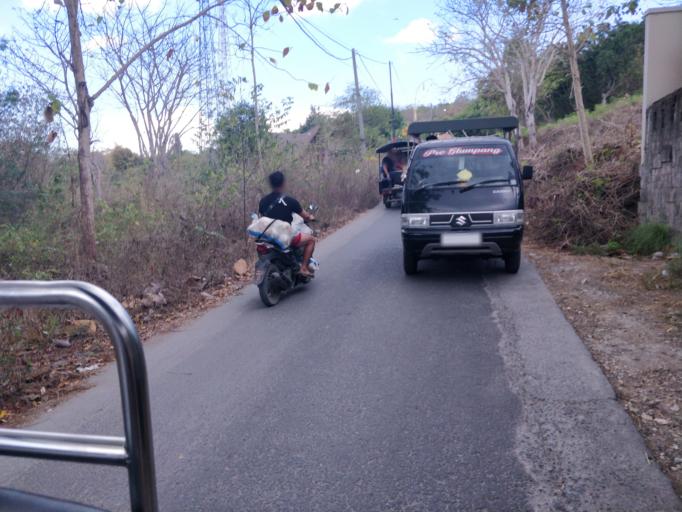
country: ID
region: Bali
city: Jungutbatu Kaja Dua
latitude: -8.6797
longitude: 115.4472
